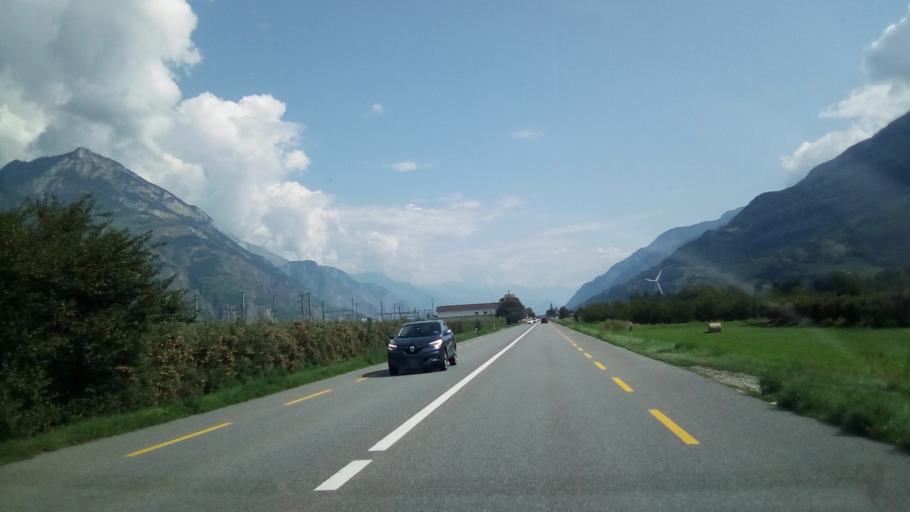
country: CH
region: Valais
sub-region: Martigny District
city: Fully
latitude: 46.1213
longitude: 7.1165
